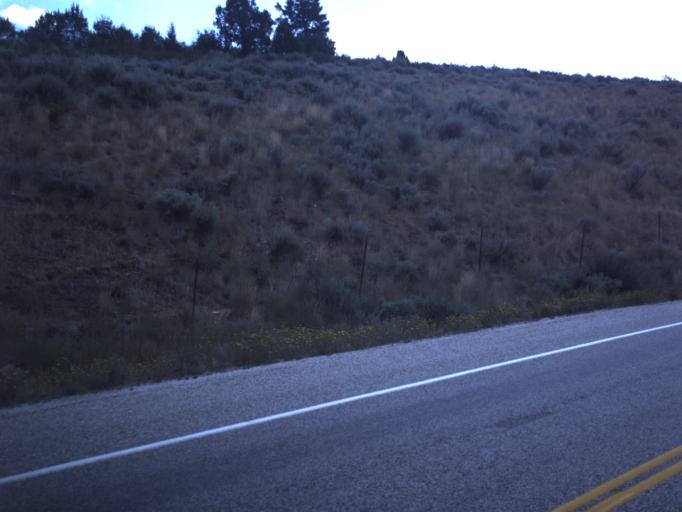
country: US
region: Idaho
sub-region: Bear Lake County
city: Paris
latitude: 41.9233
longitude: -111.4262
